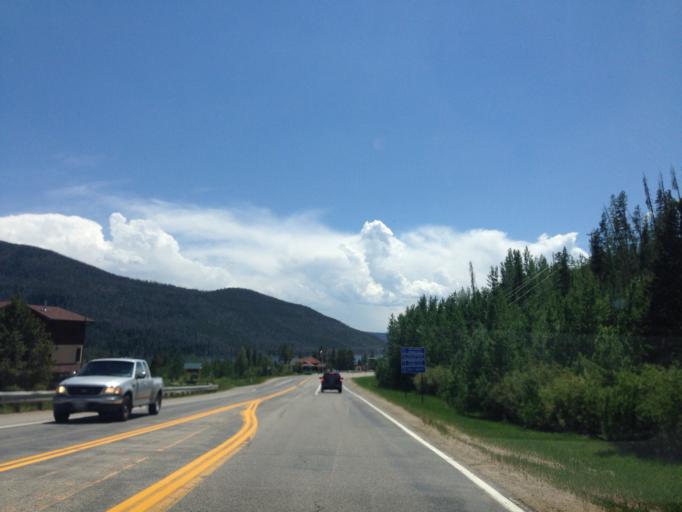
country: US
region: Colorado
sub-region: Grand County
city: Granby
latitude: 40.2541
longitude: -105.8351
